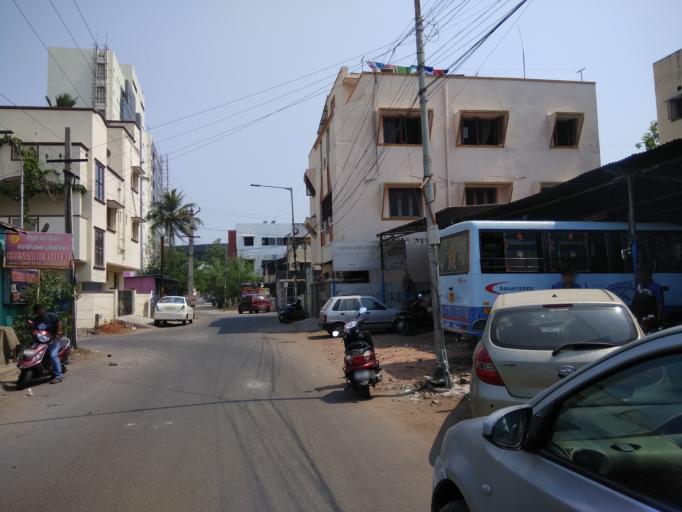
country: IN
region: Tamil Nadu
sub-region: Kancheepuram
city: Madipakkam
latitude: 12.9819
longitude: 80.1991
